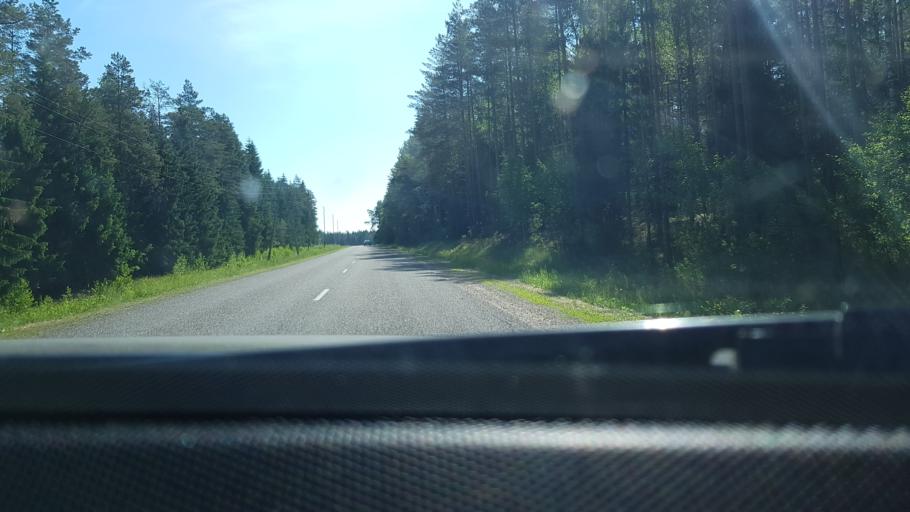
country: LV
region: Kraslavas Rajons
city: Kraslava
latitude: 55.8542
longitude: 27.0965
